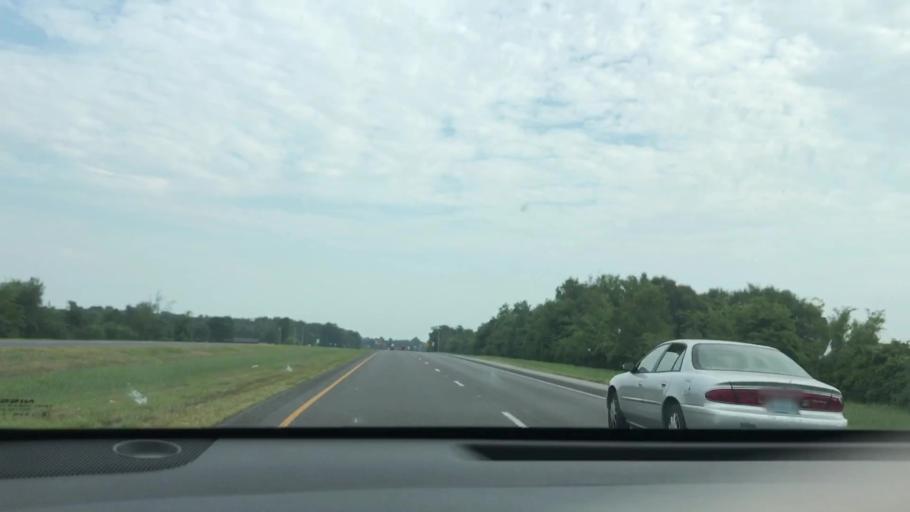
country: US
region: Kentucky
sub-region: Calloway County
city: Murray
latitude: 36.6937
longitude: -88.3031
